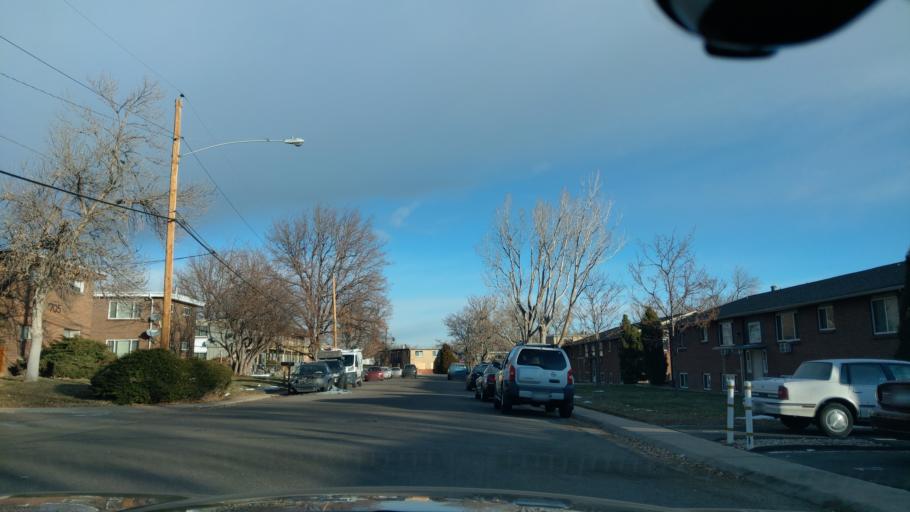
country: US
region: Colorado
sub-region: Jefferson County
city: Lakewood
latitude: 39.7278
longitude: -105.1159
